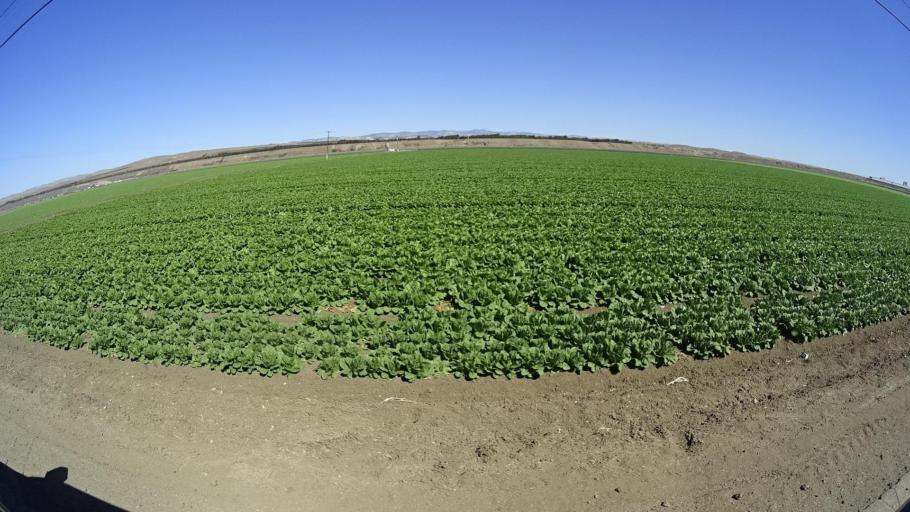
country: US
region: California
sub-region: Monterey County
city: King City
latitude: 36.2400
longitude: -121.1477
